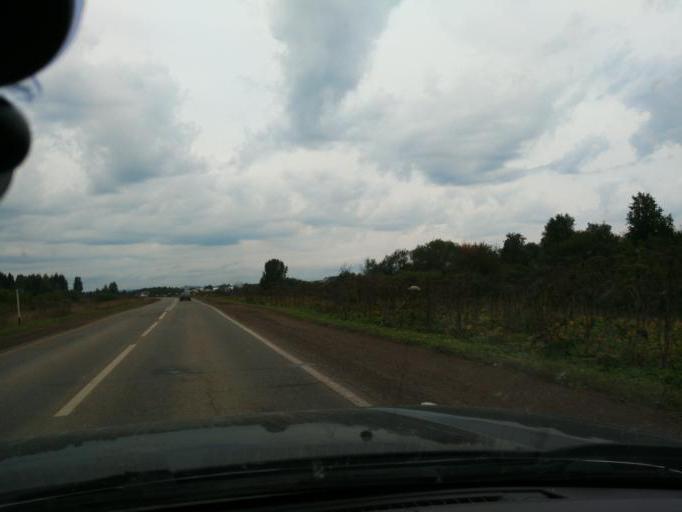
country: RU
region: Perm
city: Chernushka
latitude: 56.7259
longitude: 56.1789
